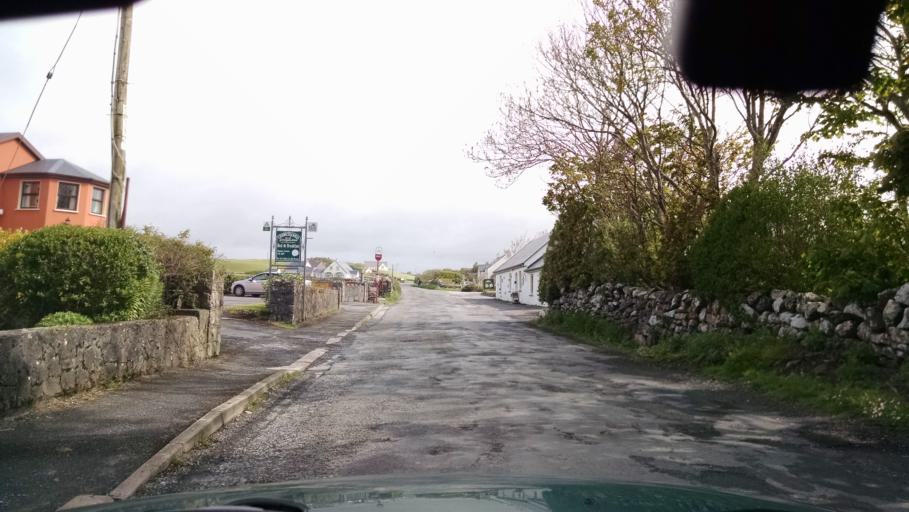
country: IE
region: Connaught
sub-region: County Galway
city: Bearna
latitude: 53.0195
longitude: -9.3711
